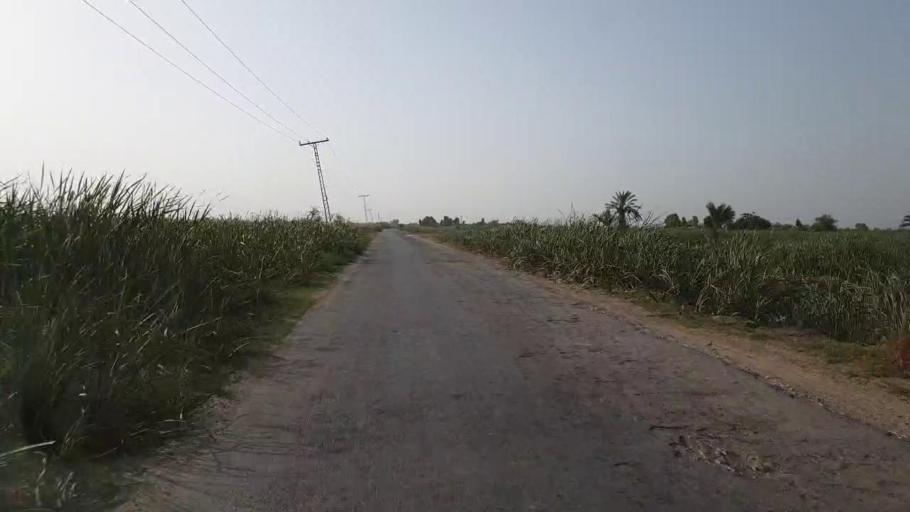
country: PK
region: Sindh
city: Jam Sahib
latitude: 26.4148
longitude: 68.8726
